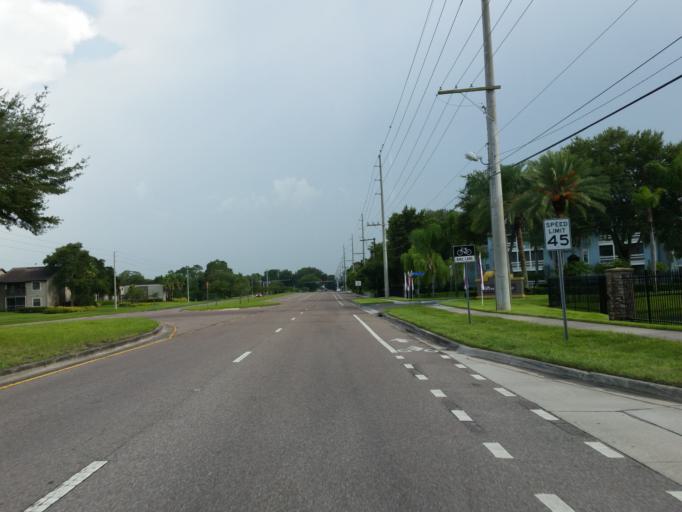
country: US
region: Florida
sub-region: Hillsborough County
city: Brandon
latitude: 27.9113
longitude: -82.3188
